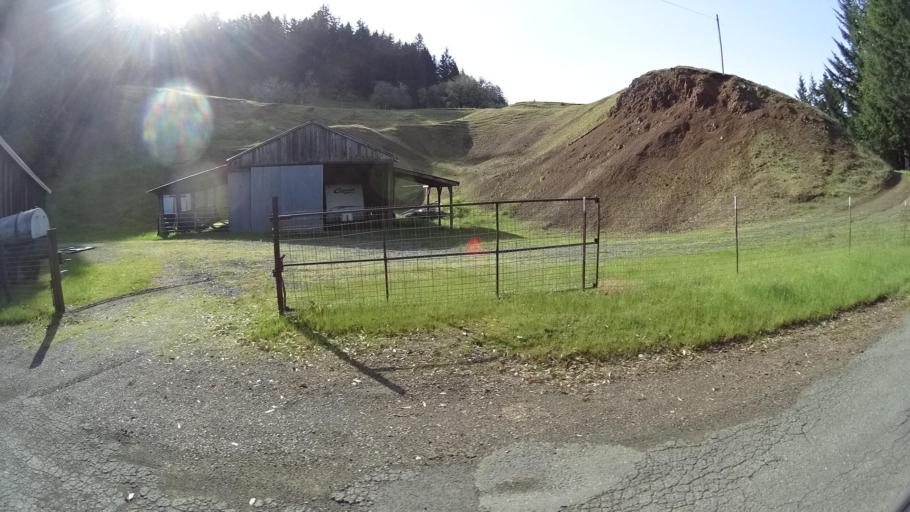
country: US
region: California
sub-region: Humboldt County
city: Hydesville
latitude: 40.6519
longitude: -123.9238
